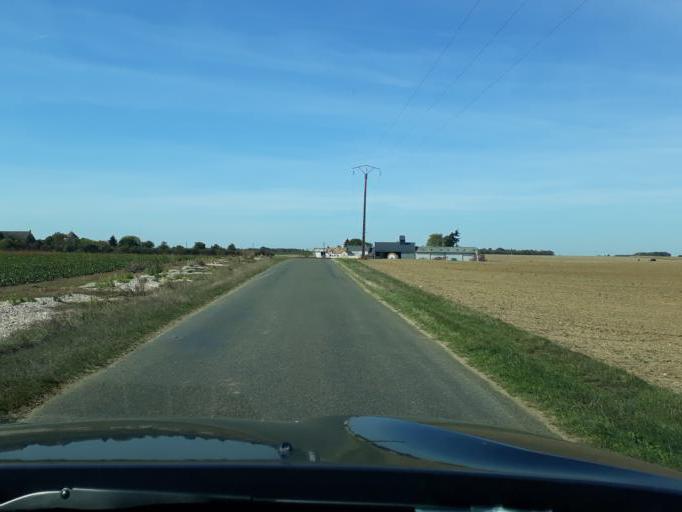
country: FR
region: Centre
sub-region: Departement du Loir-et-Cher
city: Ouzouer-le-Marche
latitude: 47.9429
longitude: 1.5306
